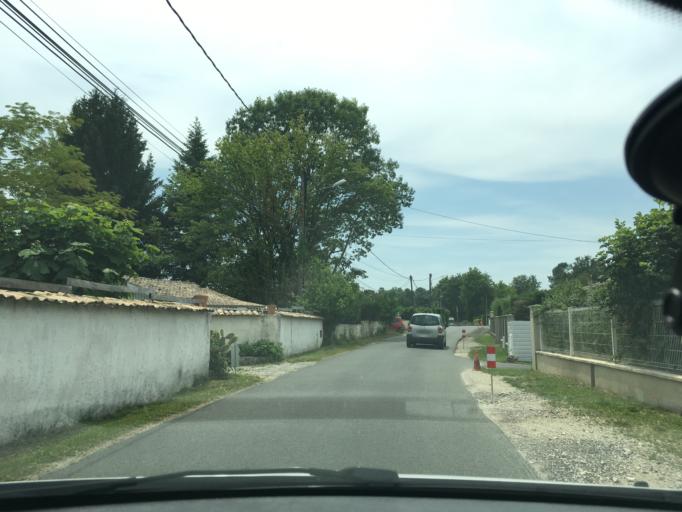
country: FR
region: Aquitaine
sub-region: Departement de la Gironde
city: Castelnau-de-Medoc
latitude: 45.0494
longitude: -0.8091
